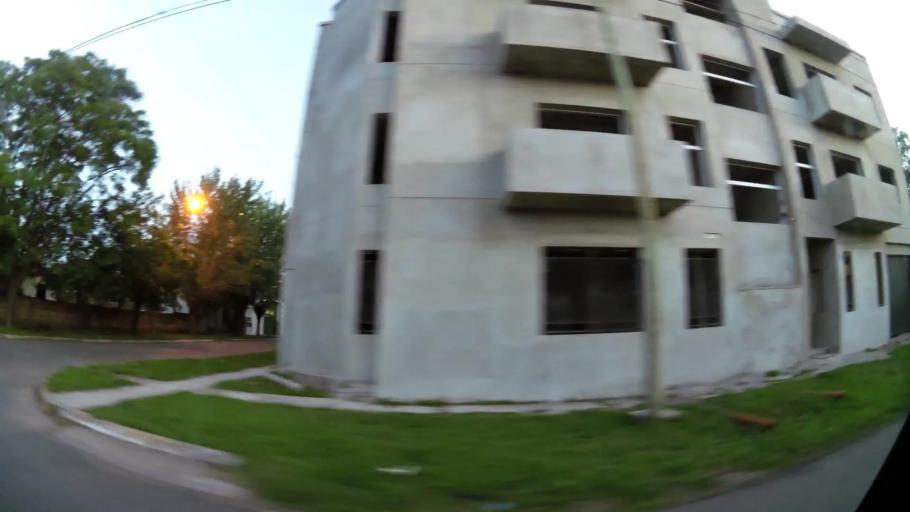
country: AR
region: Buenos Aires
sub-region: Partido de Quilmes
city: Quilmes
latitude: -34.7783
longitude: -58.2200
